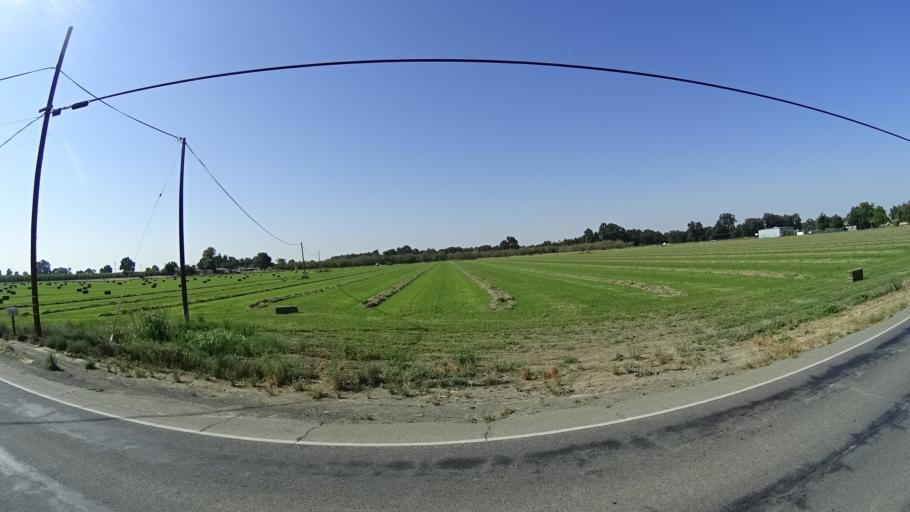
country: US
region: California
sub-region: Kings County
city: Lemoore
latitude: 36.3441
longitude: -119.8366
